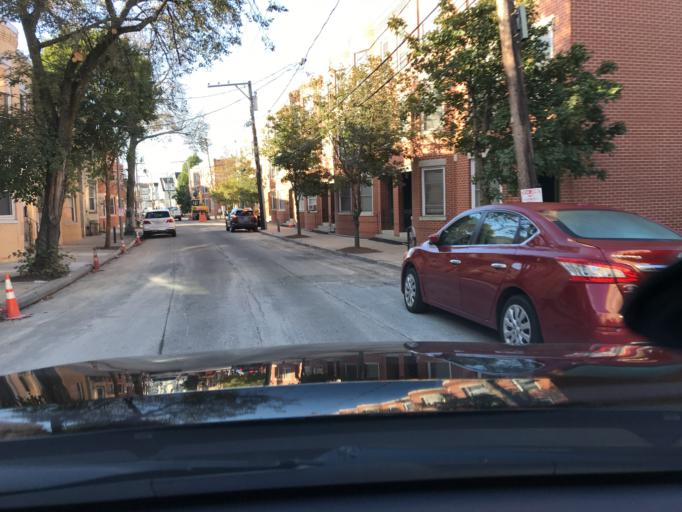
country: US
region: Massachusetts
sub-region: Suffolk County
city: Jamaica Plain
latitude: 42.3017
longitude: -71.0787
